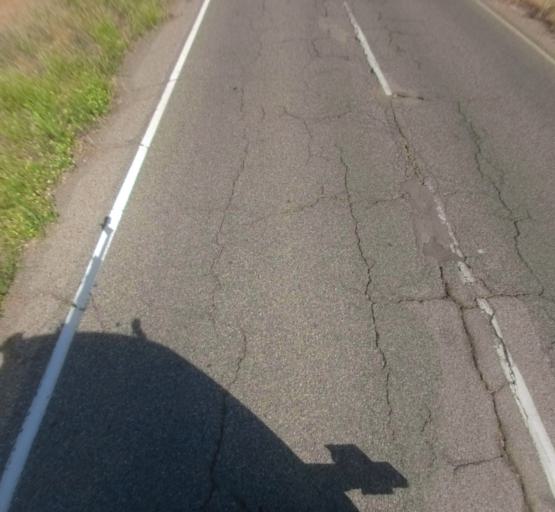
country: US
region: California
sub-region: Madera County
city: Chowchilla
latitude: 37.1385
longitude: -120.2736
